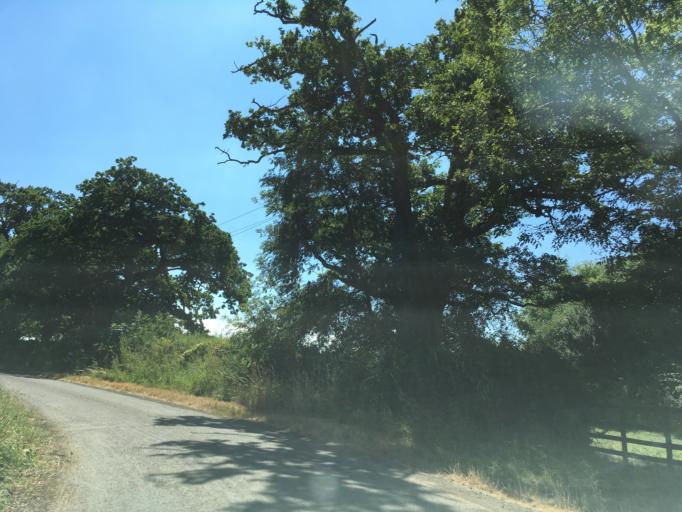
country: GB
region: England
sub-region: Wiltshire
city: Luckington
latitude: 51.5488
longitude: -2.2601
